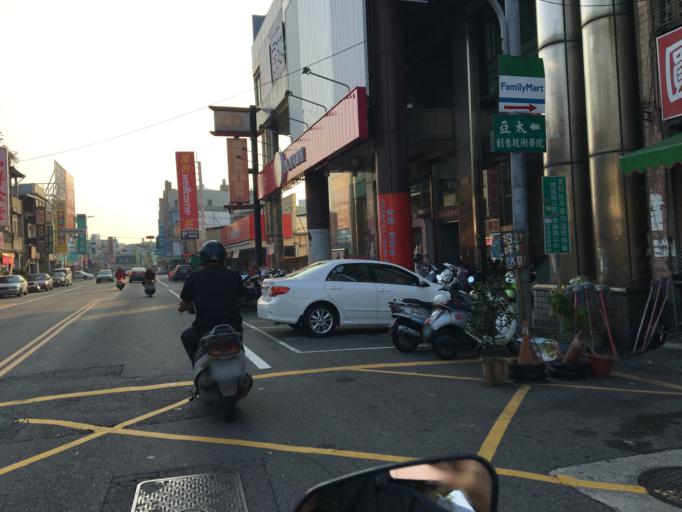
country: TW
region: Taiwan
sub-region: Hsinchu
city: Hsinchu
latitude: 24.6884
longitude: 120.9116
